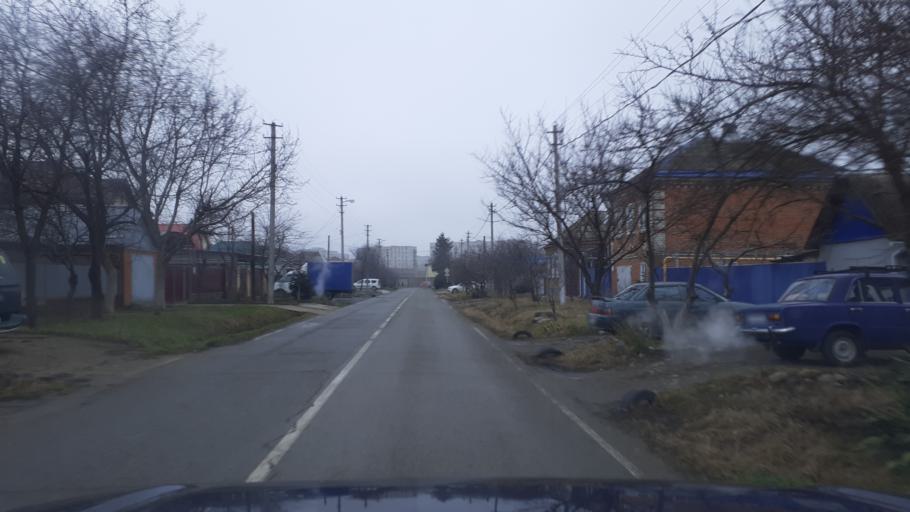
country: RU
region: Adygeya
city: Maykop
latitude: 44.6196
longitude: 40.0719
